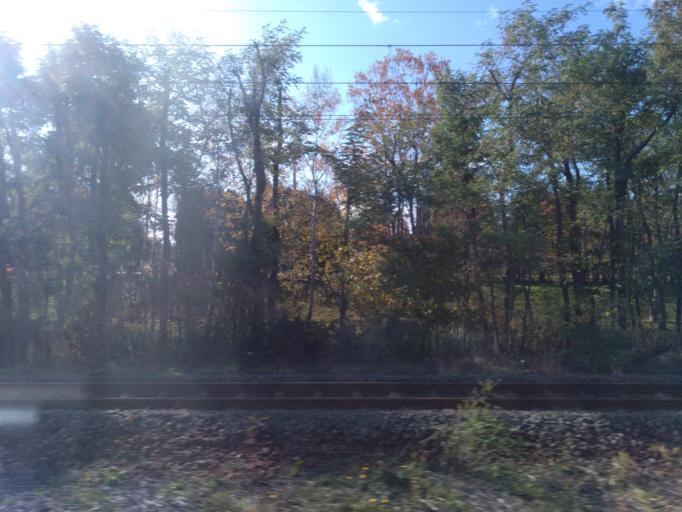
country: JP
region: Hokkaido
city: Kitahiroshima
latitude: 42.9693
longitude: 141.5660
